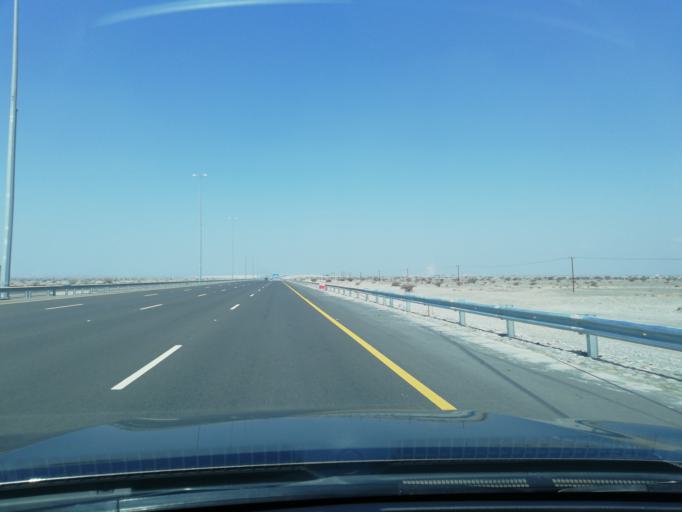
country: OM
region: Al Batinah
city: Barka'
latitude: 23.5758
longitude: 57.7679
